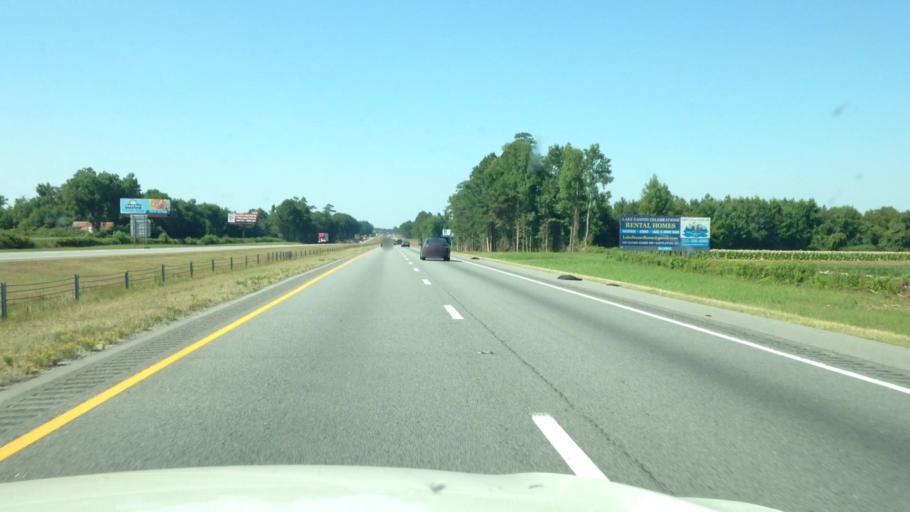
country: US
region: North Carolina
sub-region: Halifax County
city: Enfield
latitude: 36.1928
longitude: -77.7611
